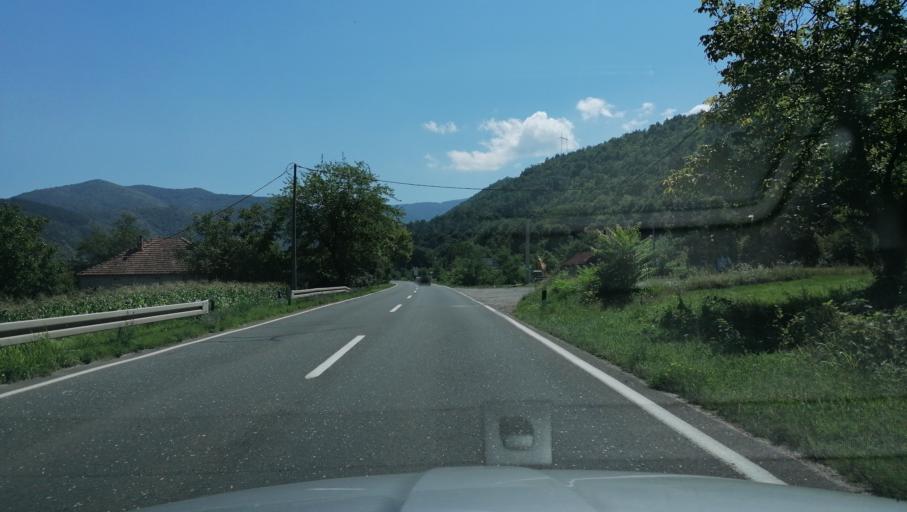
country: RS
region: Central Serbia
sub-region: Raski Okrug
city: Kraljevo
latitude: 43.6721
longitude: 20.5764
